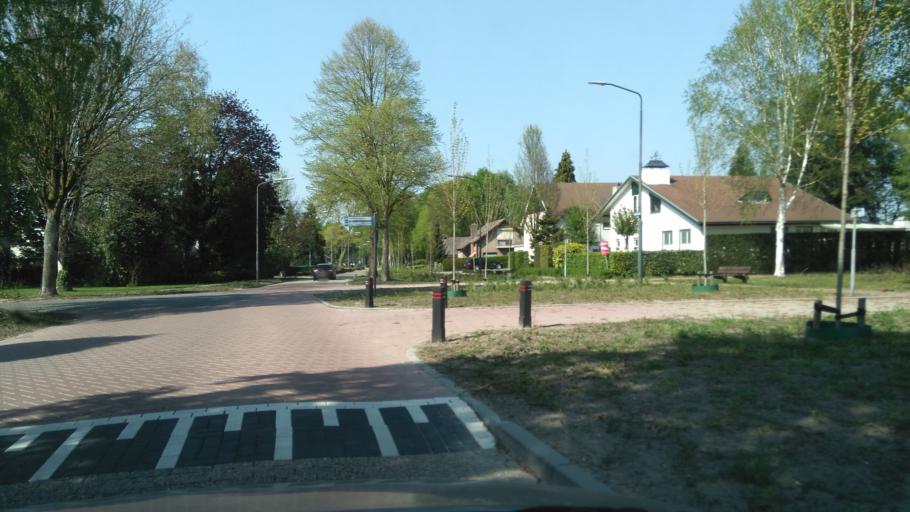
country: NL
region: North Brabant
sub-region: Gemeente Baarle-Nassau
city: Baarle-Nassau
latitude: 51.4505
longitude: 4.9317
